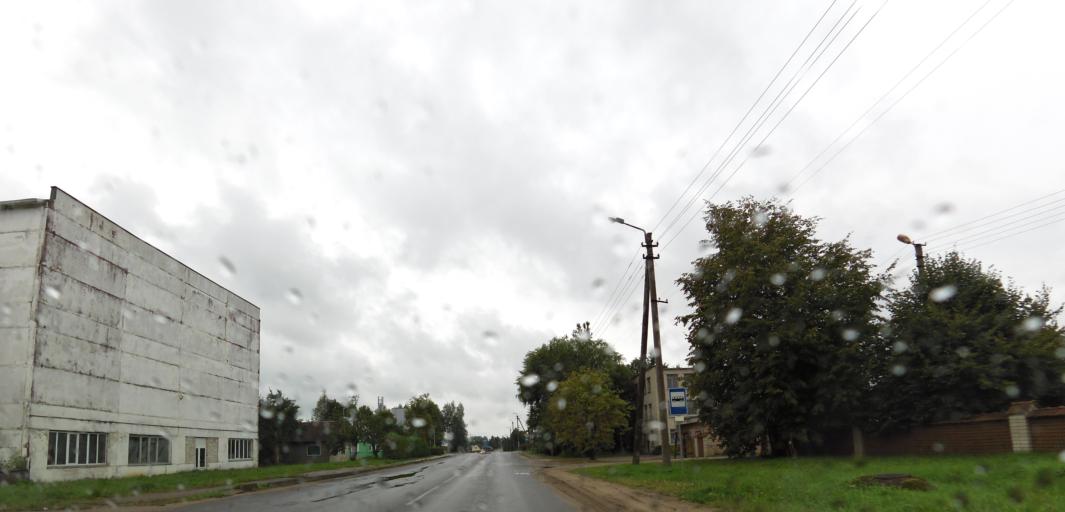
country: LT
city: Sirvintos
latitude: 55.0530
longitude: 24.9493
